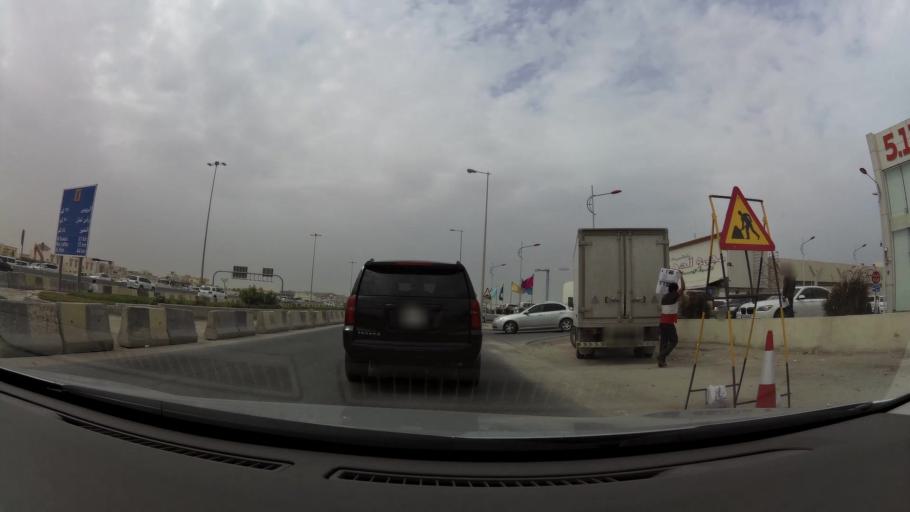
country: QA
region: Baladiyat ar Rayyan
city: Ar Rayyan
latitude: 25.3494
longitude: 51.4560
